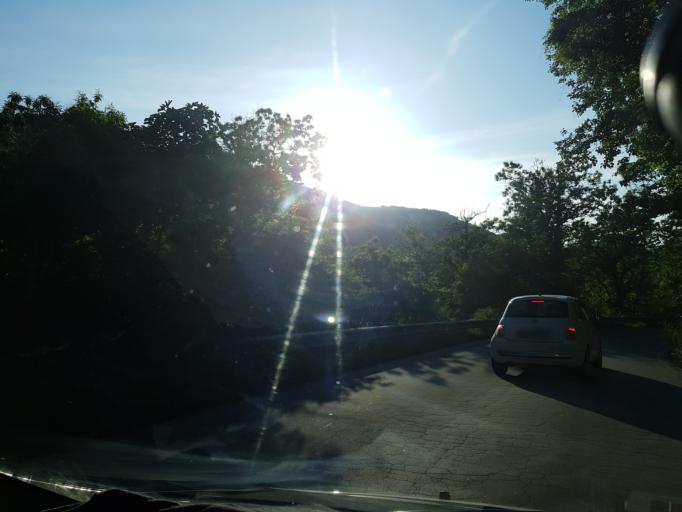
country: IT
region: Tuscany
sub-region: Provincia di Lucca
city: Minucciano
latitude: 44.1863
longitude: 10.1938
